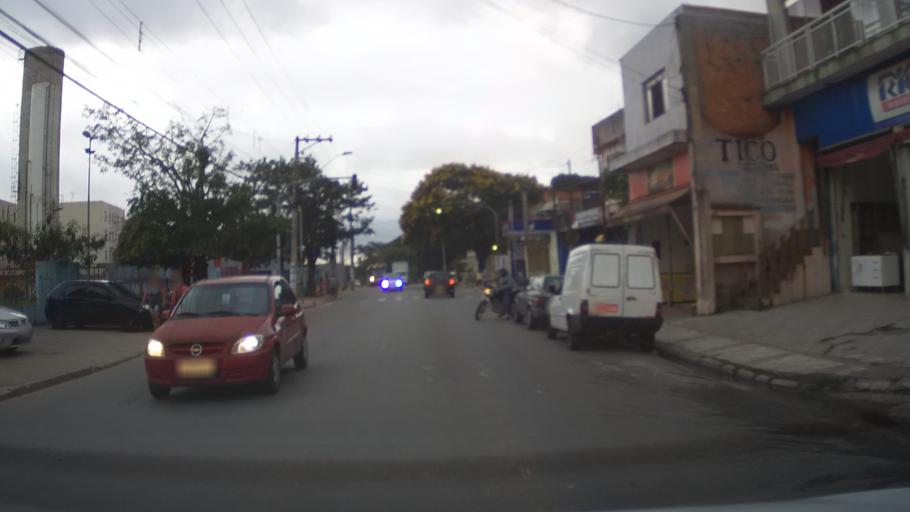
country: BR
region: Sao Paulo
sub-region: Aruja
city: Aruja
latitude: -23.4009
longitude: -46.4318
